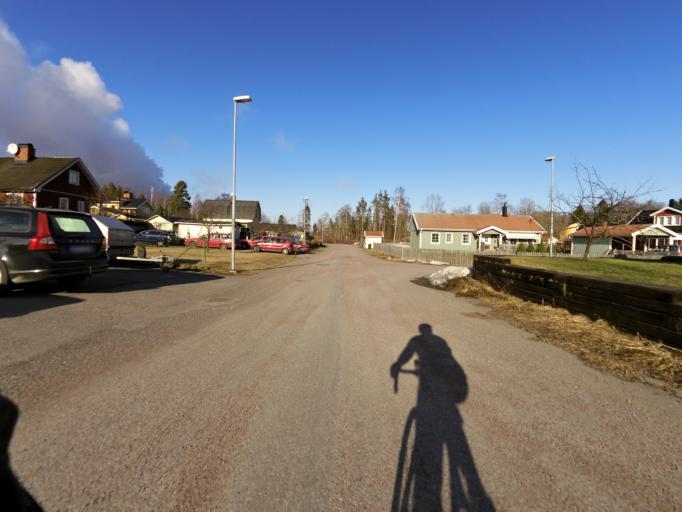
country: SE
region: Gaevleborg
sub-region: Gavle Kommun
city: Gavle
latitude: 60.6726
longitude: 17.2715
